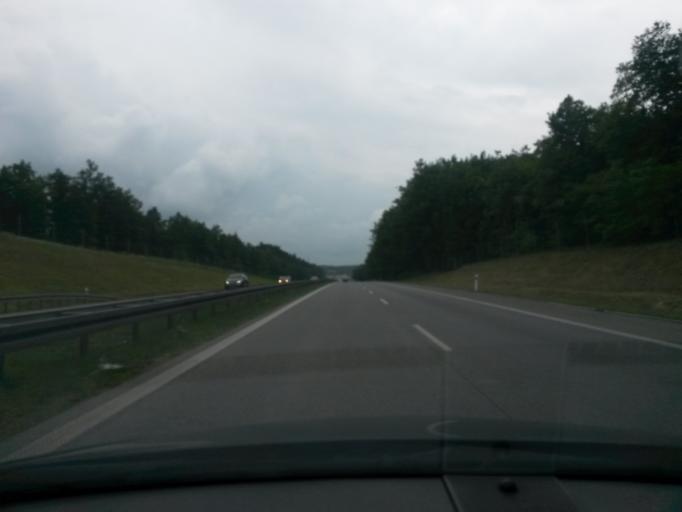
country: PL
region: Lodz Voivodeship
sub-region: Powiat skierniewicki
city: Kowiesy
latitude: 51.8342
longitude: 20.3385
